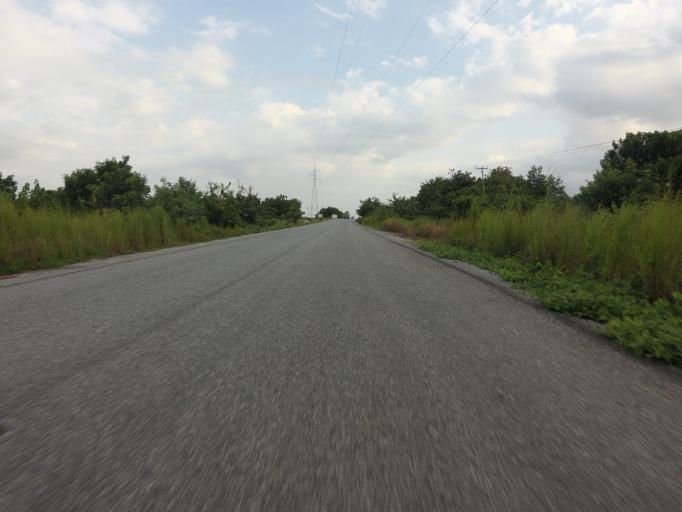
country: GH
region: Volta
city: Ho
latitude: 6.3959
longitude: 0.5258
